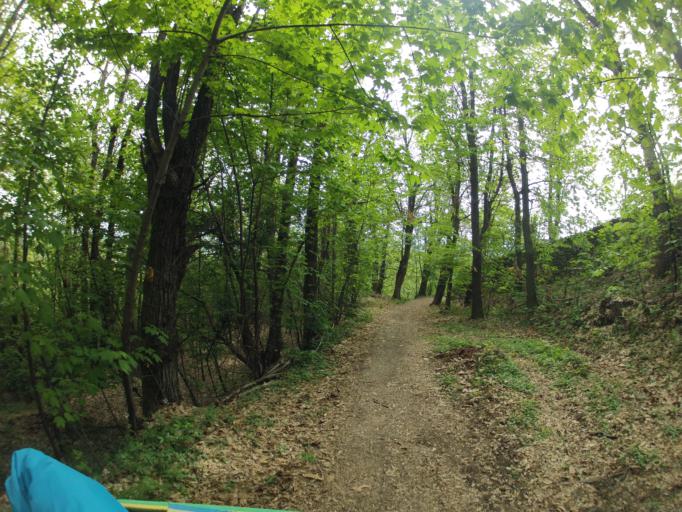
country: IT
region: Piedmont
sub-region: Provincia di Cuneo
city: Peveragno
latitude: 44.3349
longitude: 7.6179
